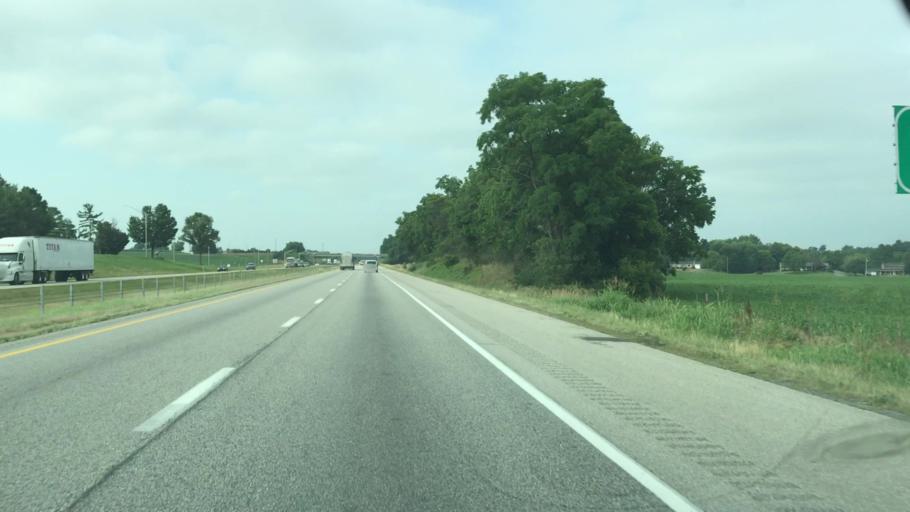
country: US
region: Pennsylvania
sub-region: Franklin County
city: Greencastle
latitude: 39.8214
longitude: -77.7013
